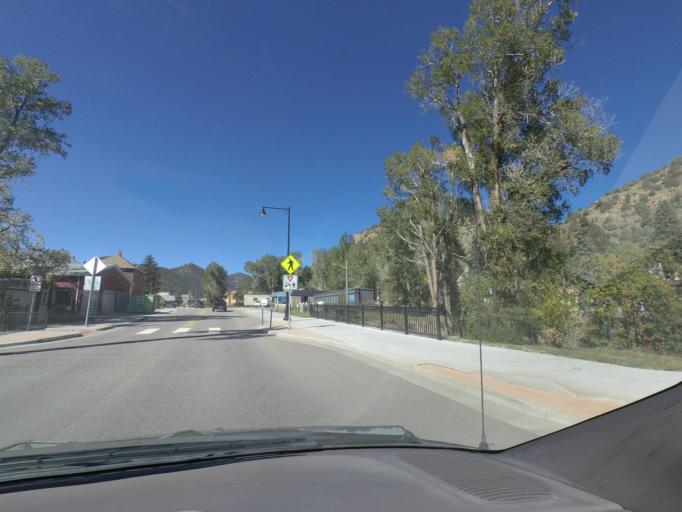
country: US
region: Colorado
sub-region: Clear Creek County
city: Idaho Springs
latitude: 39.7427
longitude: -105.5112
